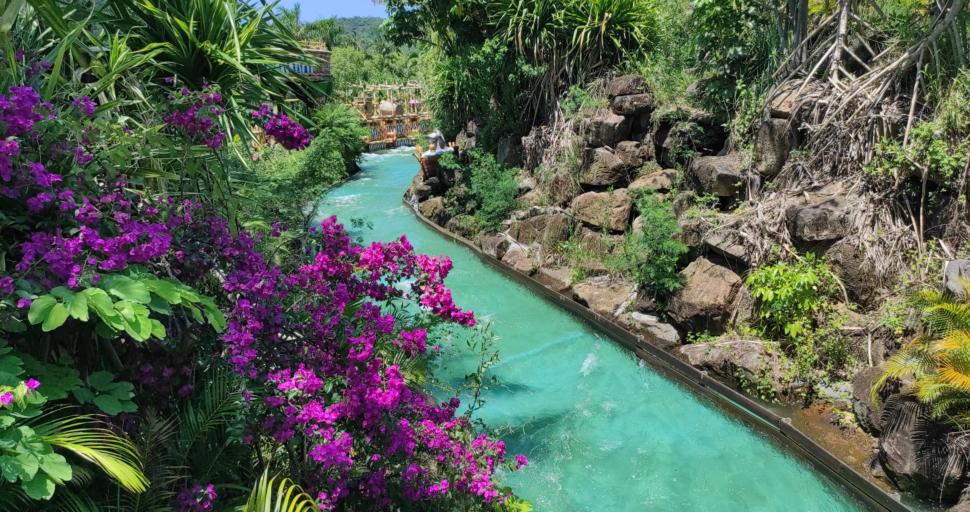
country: BR
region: Santa Catarina
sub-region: Penha
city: Penha
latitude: -26.8011
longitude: -48.6184
